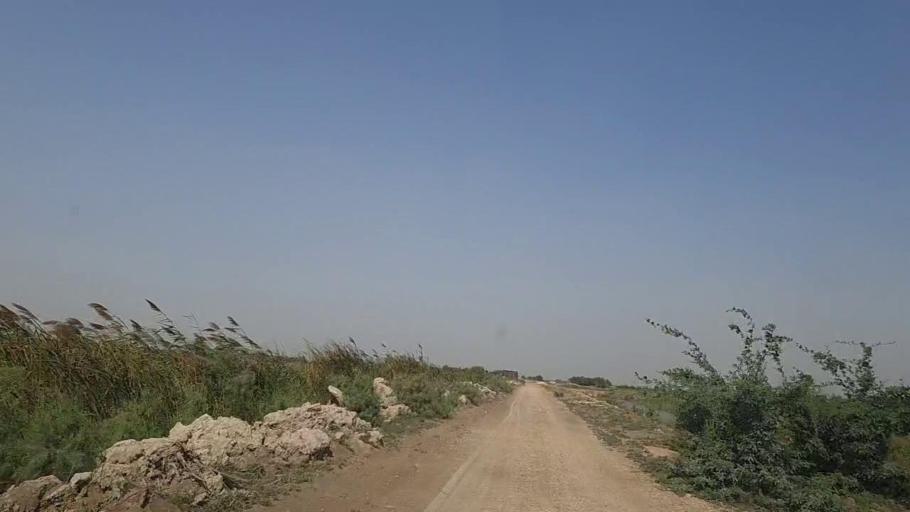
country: PK
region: Sindh
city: Daro Mehar
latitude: 24.7725
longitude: 68.1336
